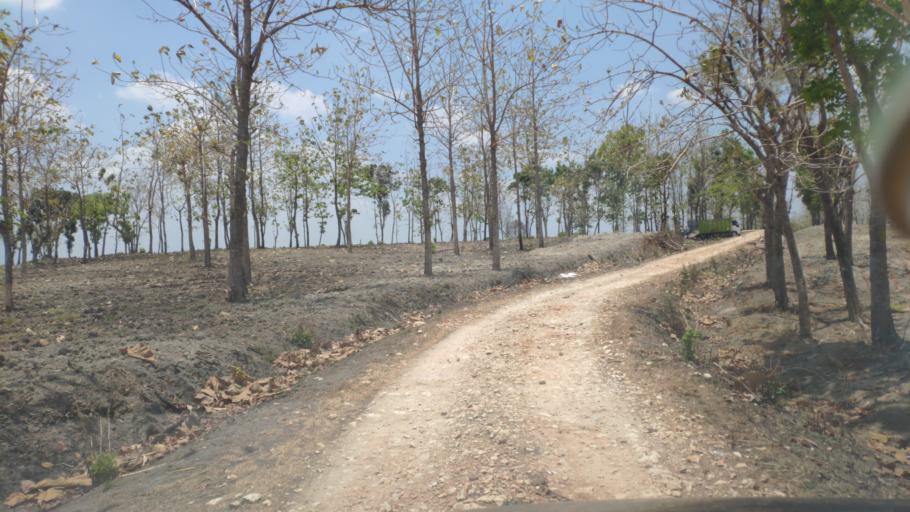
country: ID
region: West Java
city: Ngawi
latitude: -7.3245
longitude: 111.3587
